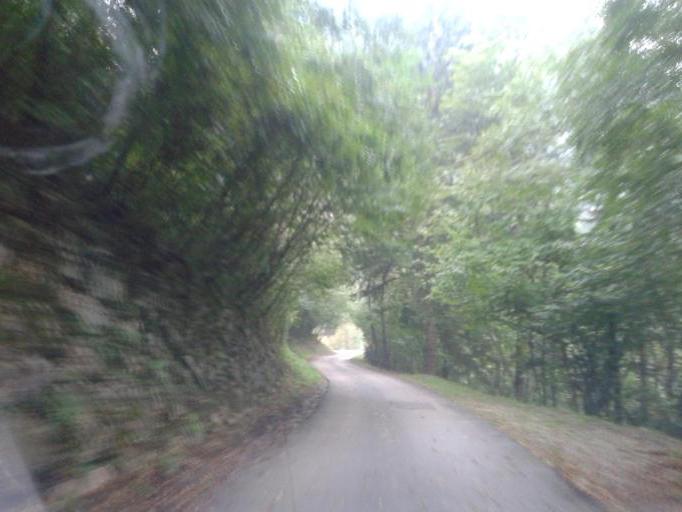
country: IT
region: Trentino-Alto Adige
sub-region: Provincia di Trento
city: Storo
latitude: 45.8408
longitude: 10.6140
